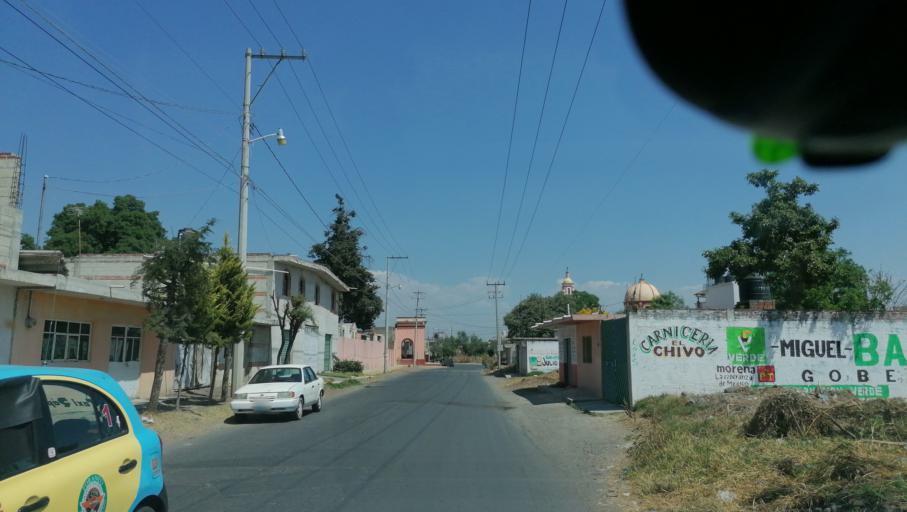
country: MX
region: Puebla
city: Huejotzingo
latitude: 19.1667
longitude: -98.4114
